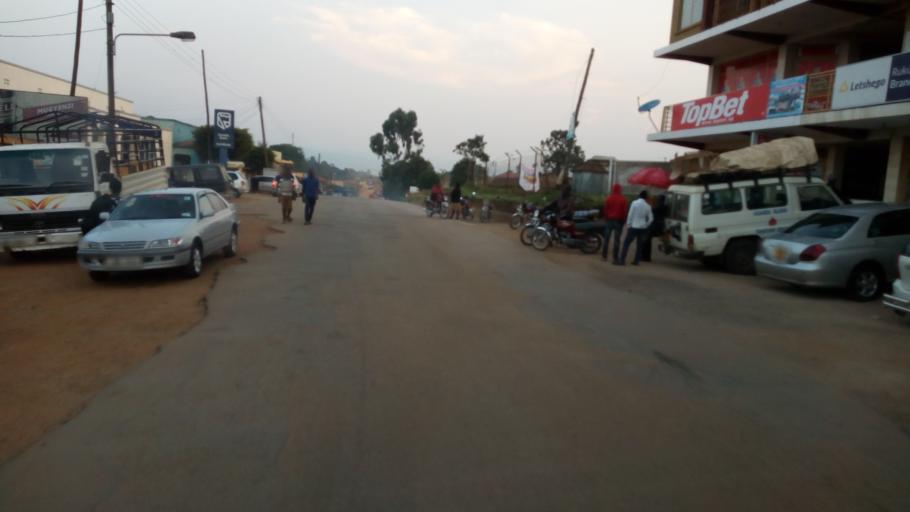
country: UG
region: Western Region
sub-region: Rukungiri District
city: Rukungiri
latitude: -0.7925
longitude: 29.9254
